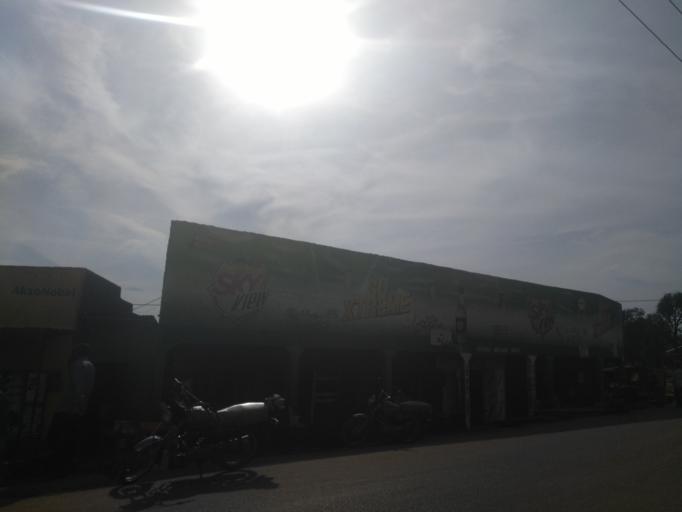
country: UG
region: Central Region
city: Kampala Central Division
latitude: 0.3539
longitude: 32.5684
